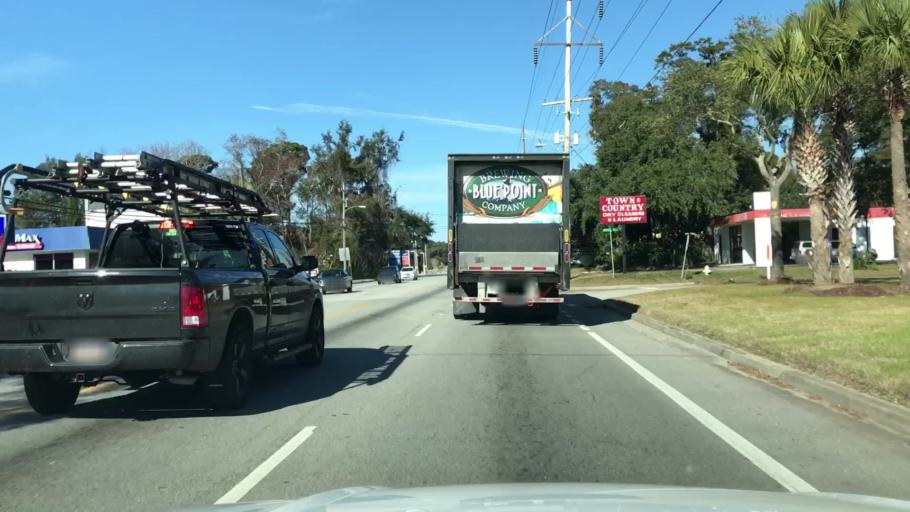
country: US
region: South Carolina
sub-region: Charleston County
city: Charleston
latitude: 32.7416
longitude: -79.9679
